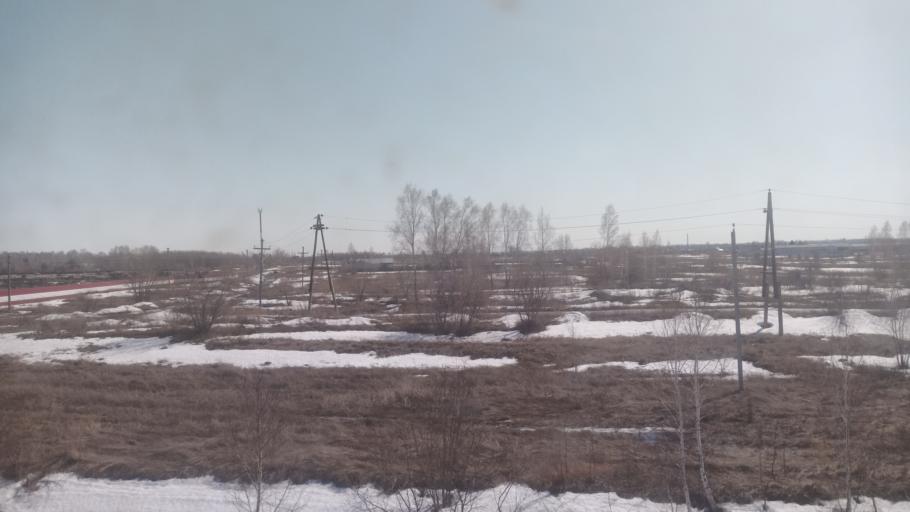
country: RU
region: Altai Krai
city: Beloyarsk
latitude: 53.4484
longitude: 83.9705
